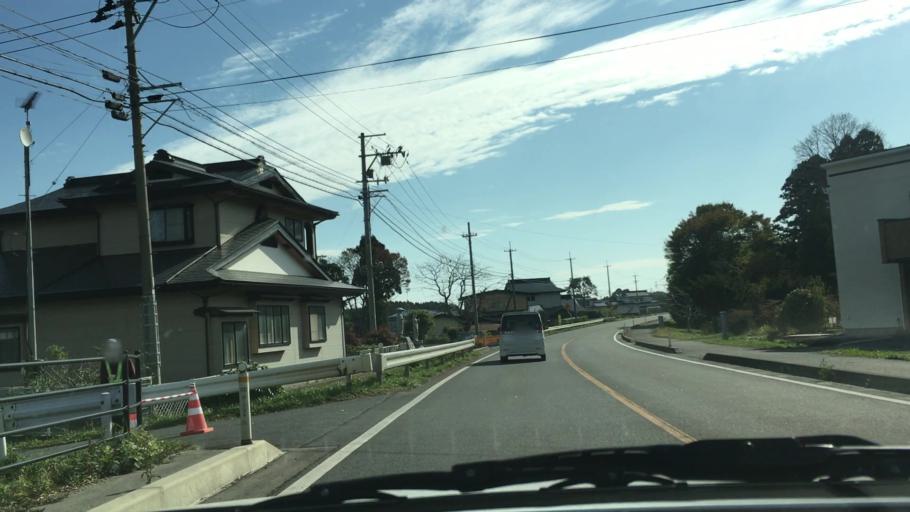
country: JP
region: Aomori
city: Hachinohe
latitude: 40.4261
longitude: 141.6958
